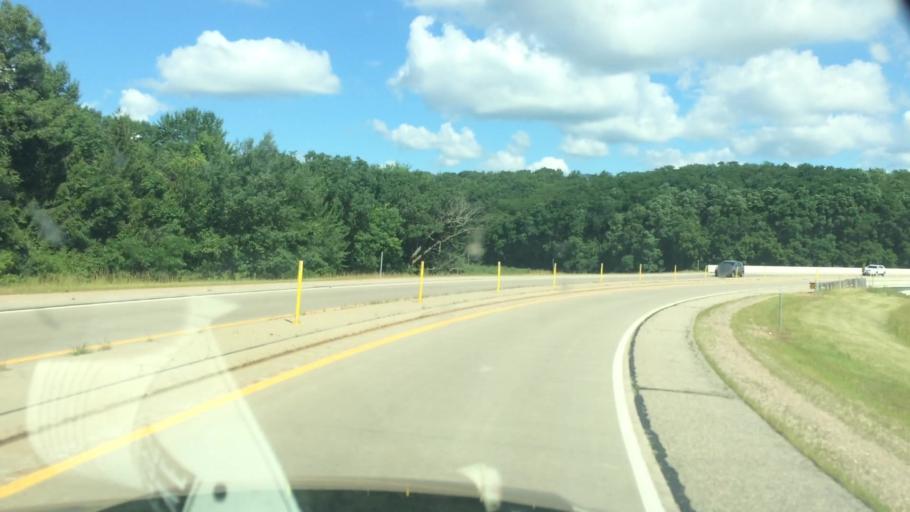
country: US
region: Wisconsin
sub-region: Waupaca County
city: Waupaca
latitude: 44.3368
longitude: -89.0696
